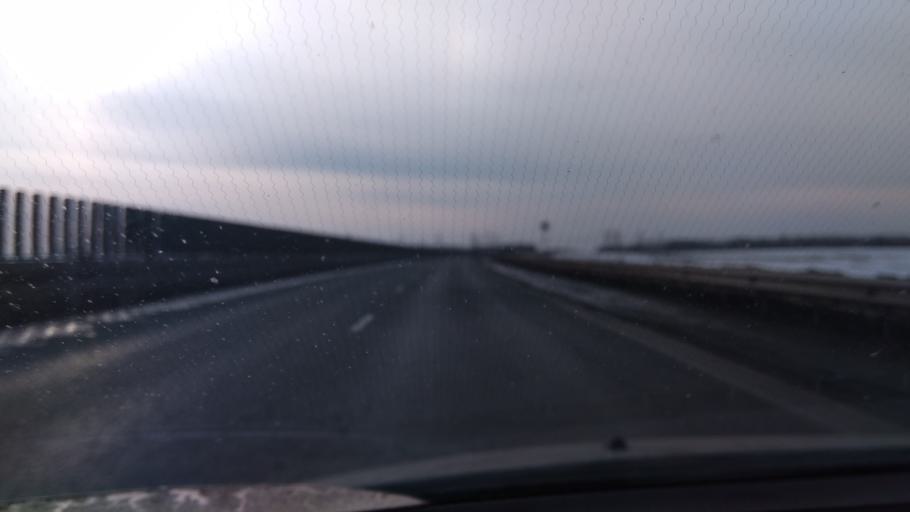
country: RU
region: Perm
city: Ferma
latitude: 57.9301
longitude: 56.3207
